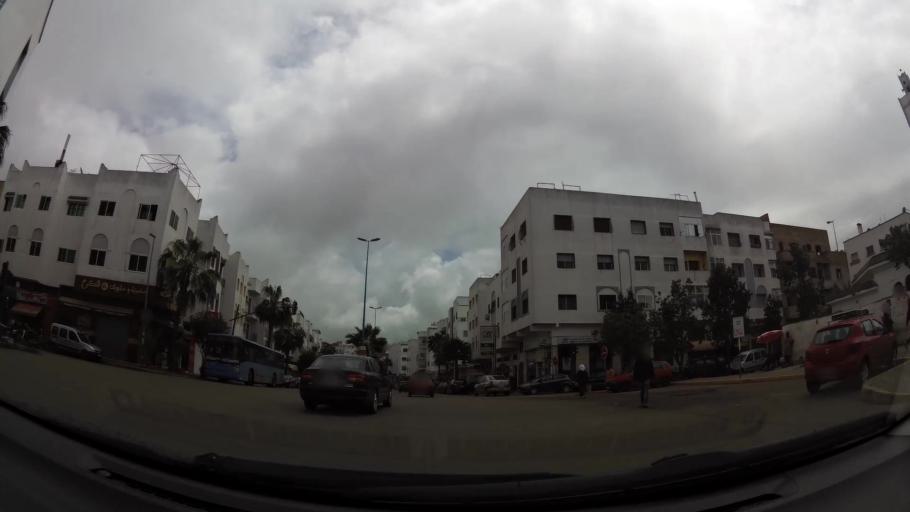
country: MA
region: Grand Casablanca
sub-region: Casablanca
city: Casablanca
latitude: 33.5409
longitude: -7.6832
